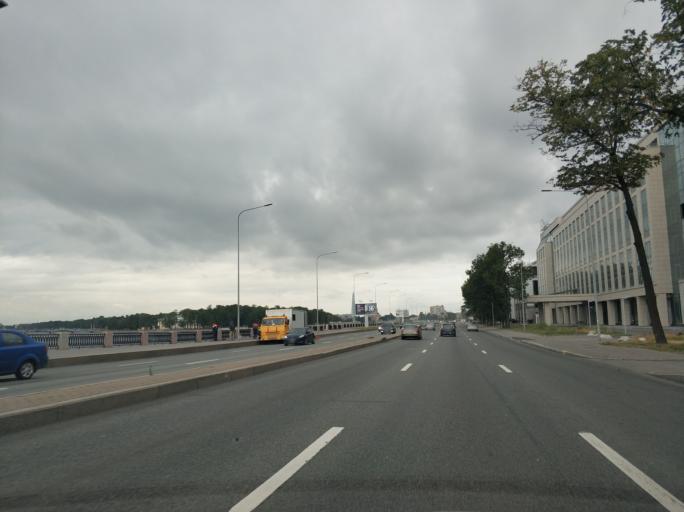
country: RU
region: Leningrad
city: Chernaya Rechka
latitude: 59.9812
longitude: 30.3164
